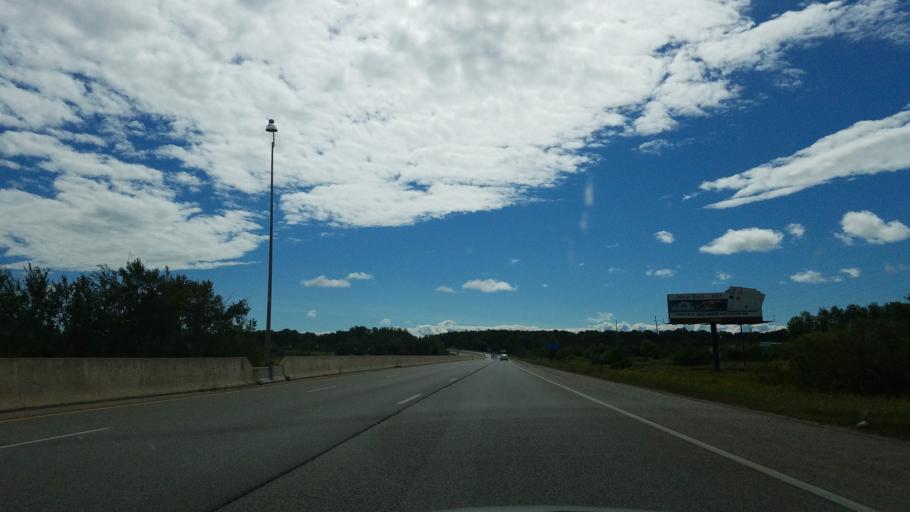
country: US
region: Michigan
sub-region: Chippewa County
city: Sault Ste. Marie
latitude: 46.4892
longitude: -84.3744
